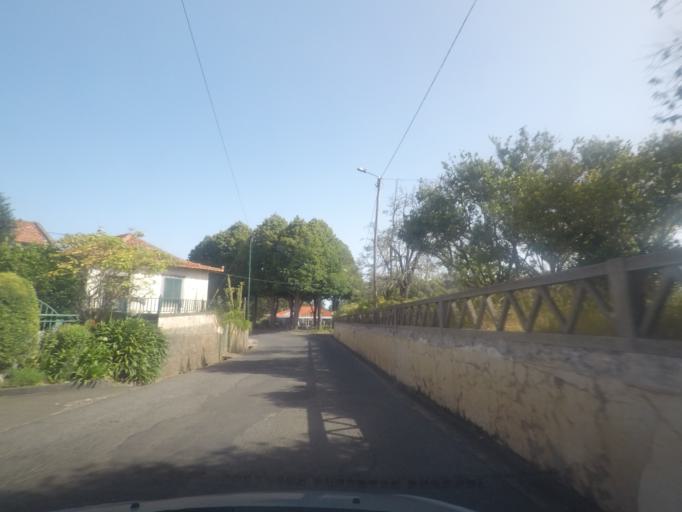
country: PT
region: Madeira
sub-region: Calheta
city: Estreito da Calheta
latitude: 32.7552
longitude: -17.2015
